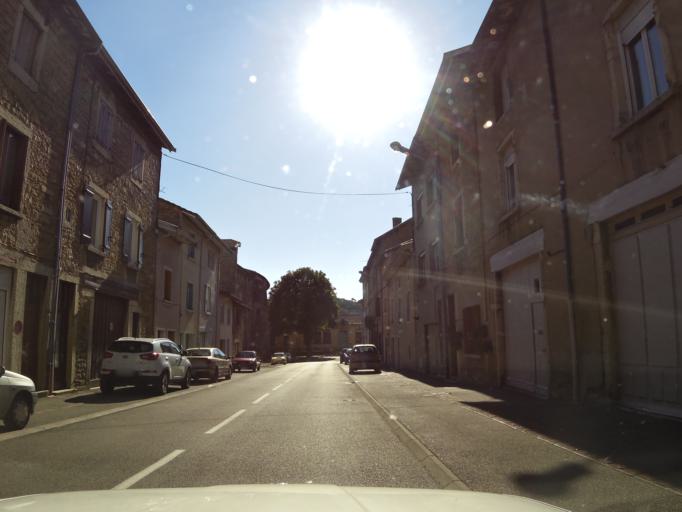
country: FR
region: Rhone-Alpes
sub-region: Departement de l'Ain
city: Lagnieu
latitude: 45.9044
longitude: 5.3466
